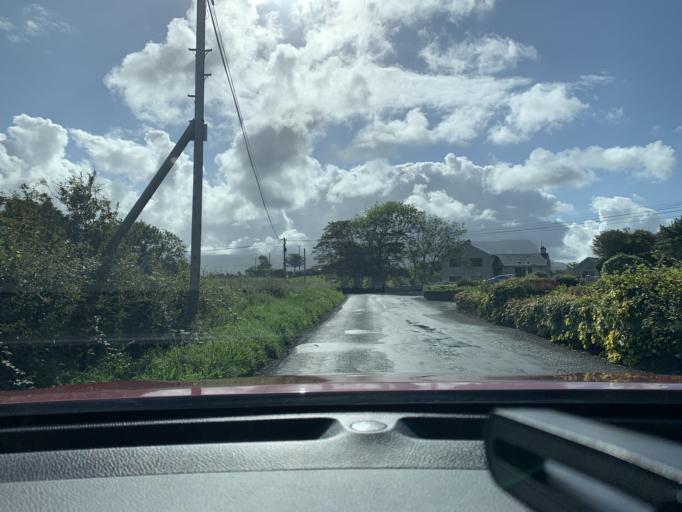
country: IE
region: Connaught
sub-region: Sligo
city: Strandhill
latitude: 54.3914
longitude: -8.5444
